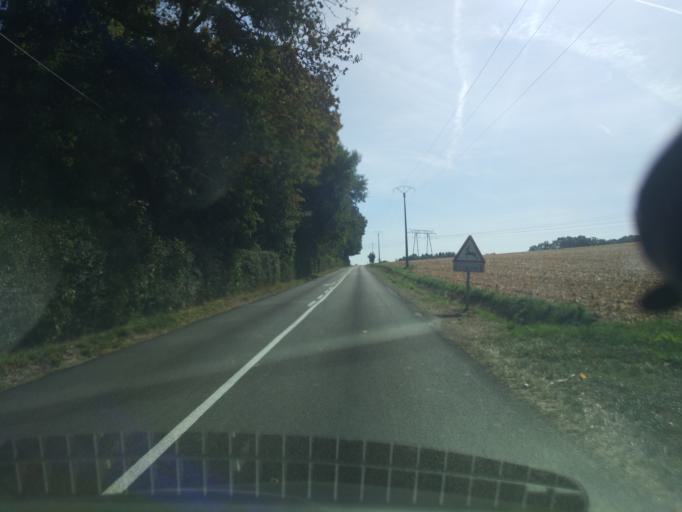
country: FR
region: Ile-de-France
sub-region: Departement de l'Essonne
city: Forges-les-Bains
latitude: 48.6395
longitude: 2.1012
